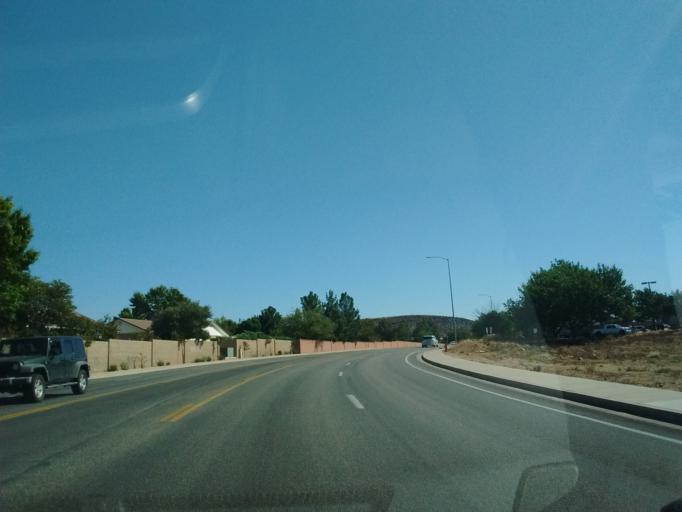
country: US
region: Utah
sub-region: Washington County
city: Saint George
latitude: 37.0885
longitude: -113.5599
